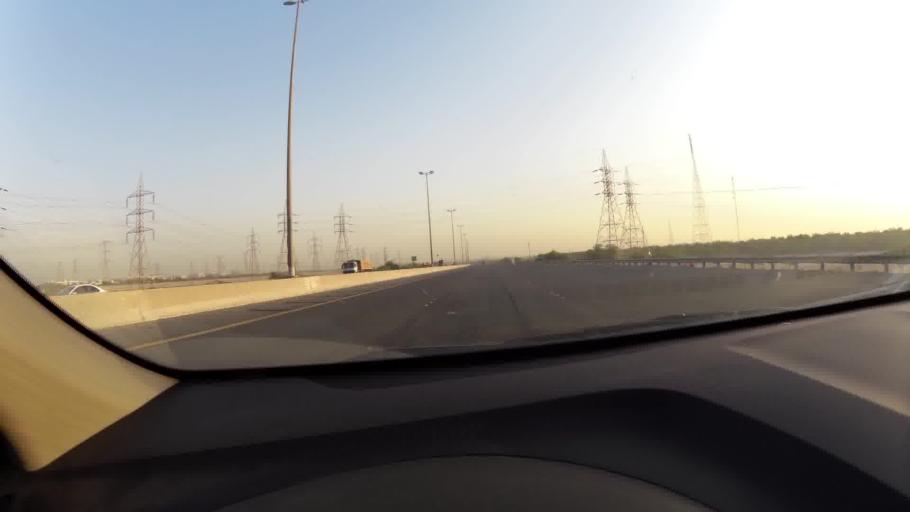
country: KW
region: Al Ahmadi
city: Al Ahmadi
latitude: 29.0746
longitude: 48.0997
